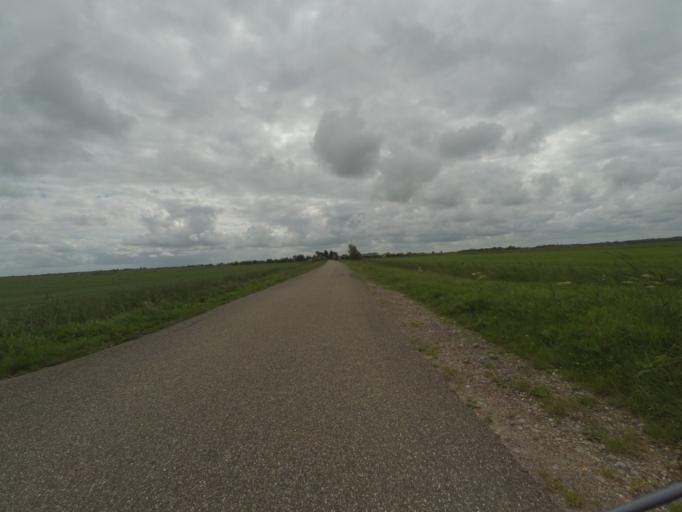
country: NL
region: Friesland
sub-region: Gemeente Kollumerland en Nieuwkruisland
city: Kollumerzwaag
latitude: 53.3125
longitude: 6.0895
